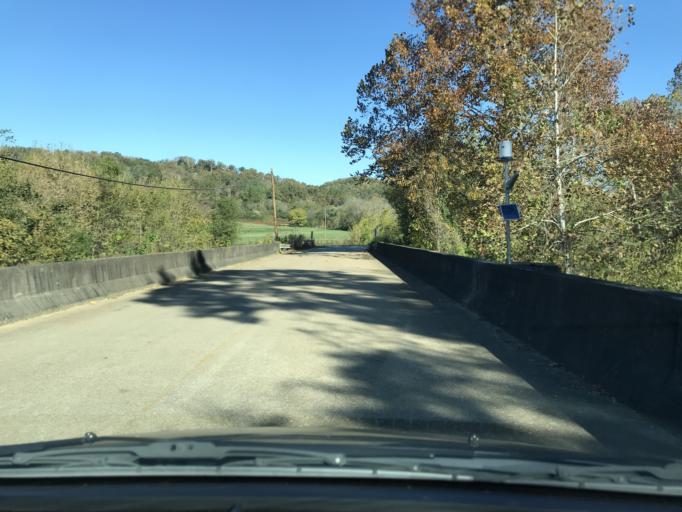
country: US
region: Georgia
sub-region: Dade County
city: Trenton
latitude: 34.8969
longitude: -85.4636
